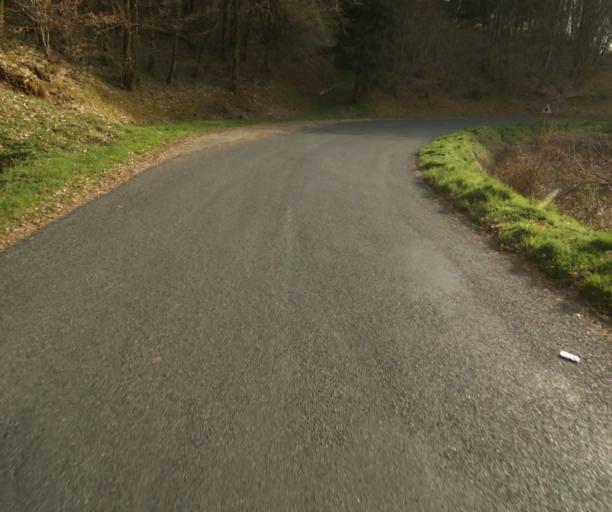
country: FR
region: Limousin
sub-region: Departement de la Correze
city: Naves
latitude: 45.3458
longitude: 1.8144
